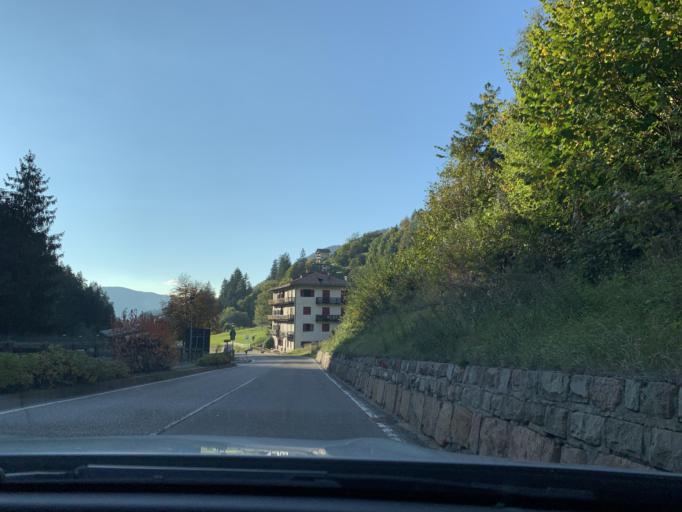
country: IT
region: Trentino-Alto Adige
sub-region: Bolzano
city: Nova Levante
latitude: 46.4275
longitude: 11.5369
